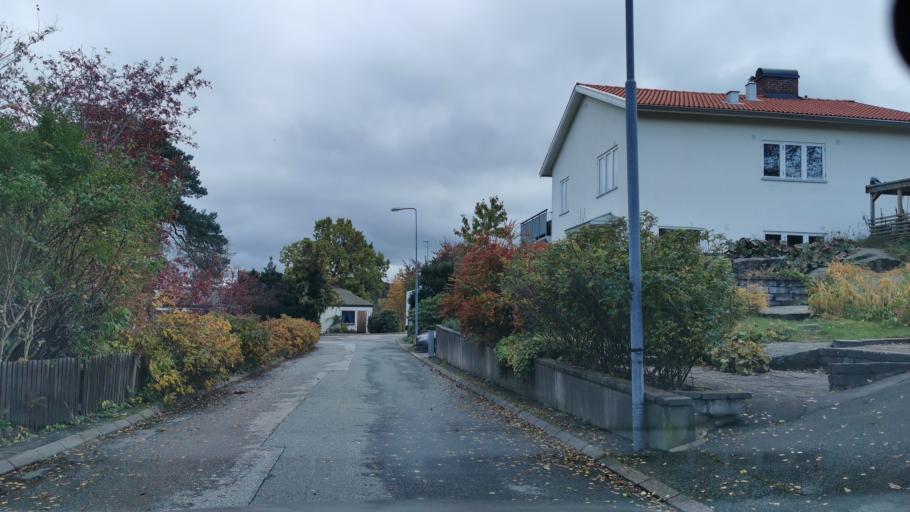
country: SE
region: Vaestra Goetaland
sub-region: Partille Kommun
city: Partille
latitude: 57.7251
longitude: 12.0726
